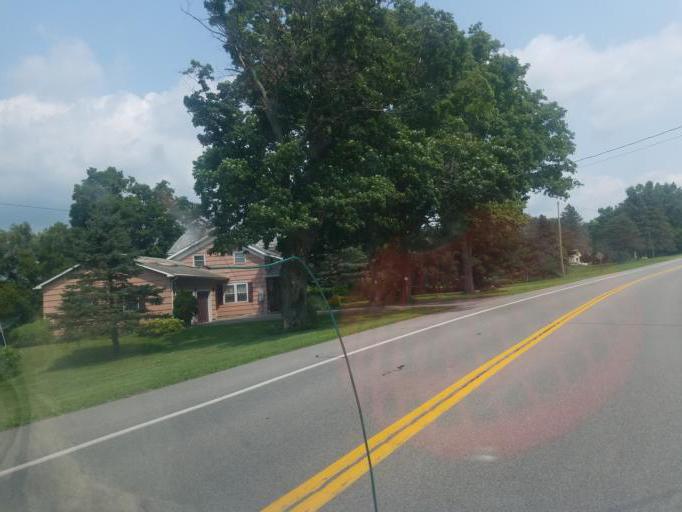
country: US
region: New York
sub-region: Herkimer County
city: Little Falls
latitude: 43.0168
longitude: -74.8914
